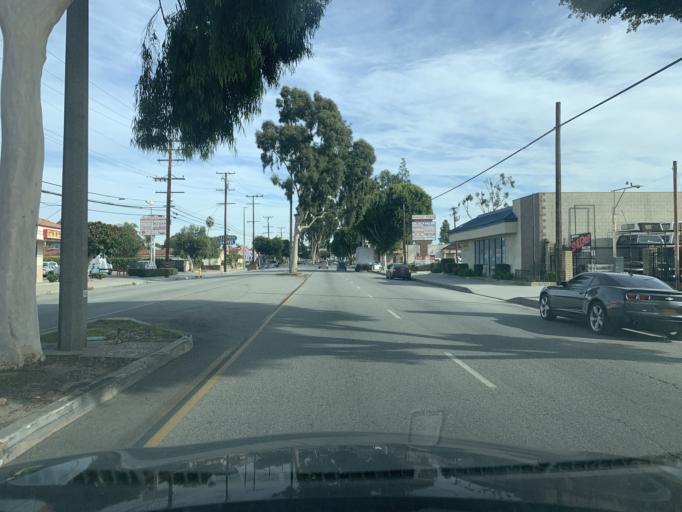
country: US
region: California
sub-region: Los Angeles County
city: South El Monte
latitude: 34.0627
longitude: -118.0459
